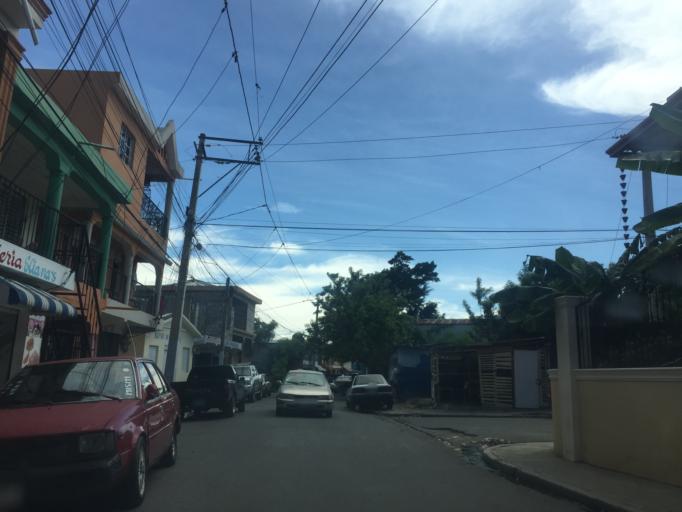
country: DO
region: Santiago
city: Santiago de los Caballeros
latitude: 19.4318
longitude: -70.6773
